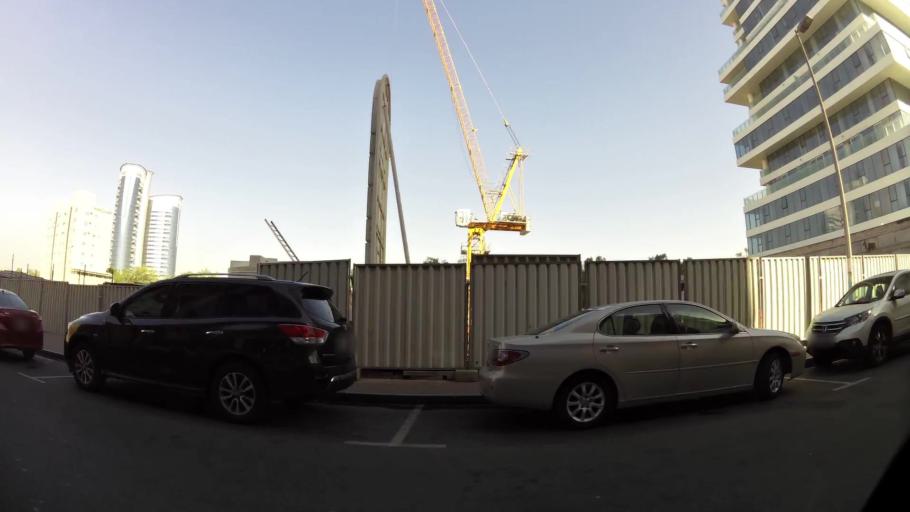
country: AE
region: Ash Shariqah
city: Sharjah
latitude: 25.2522
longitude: 55.2924
